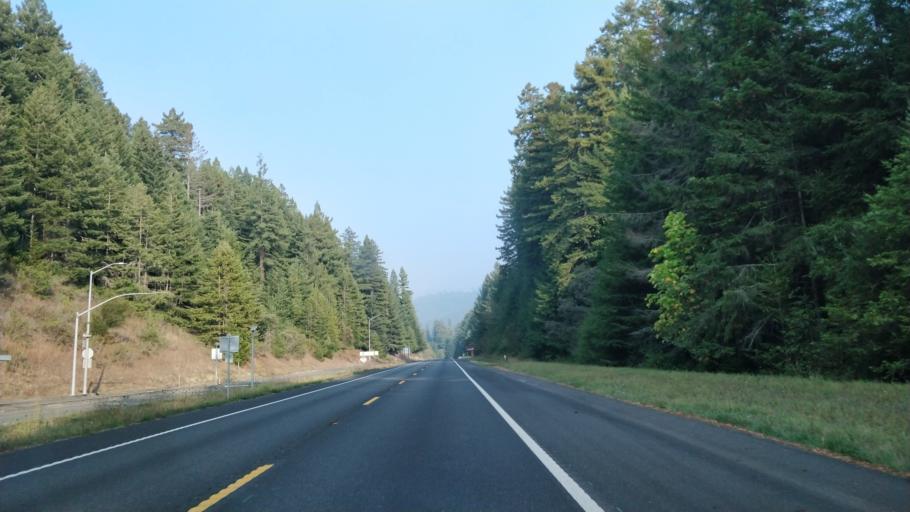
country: US
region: California
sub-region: Humboldt County
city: Blue Lake
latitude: 40.8844
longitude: -123.9632
